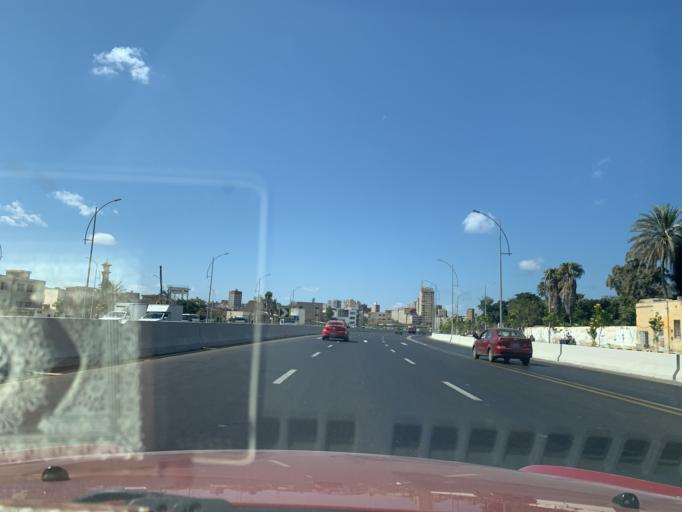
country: EG
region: Alexandria
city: Alexandria
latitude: 31.2002
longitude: 29.9485
